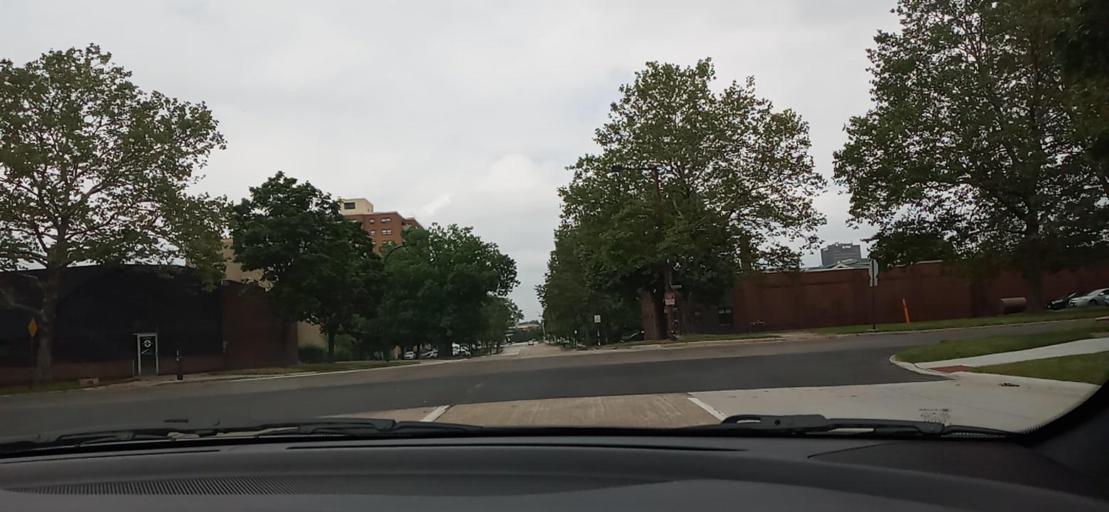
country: US
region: Ohio
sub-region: Summit County
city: Akron
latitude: 41.0748
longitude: -81.5292
